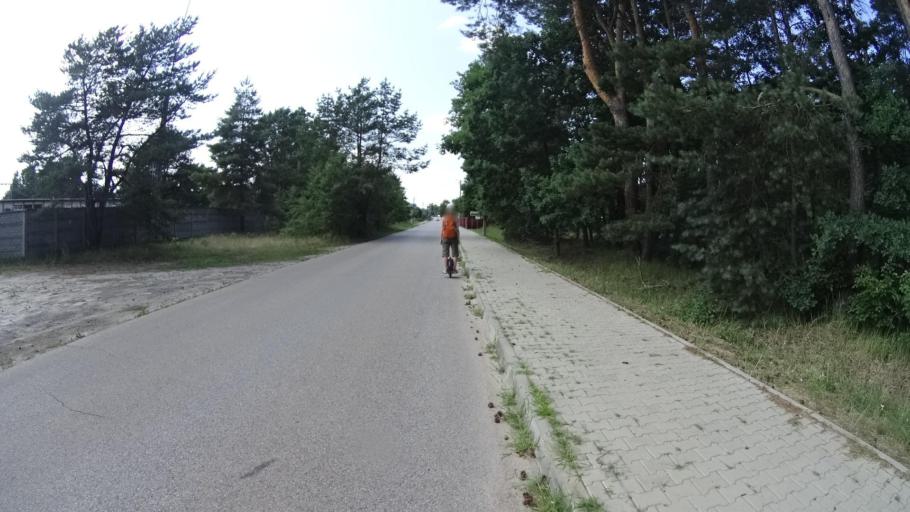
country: PL
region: Masovian Voivodeship
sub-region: Powiat bialobrzeski
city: Bialobrzegi
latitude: 51.6450
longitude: 20.9648
